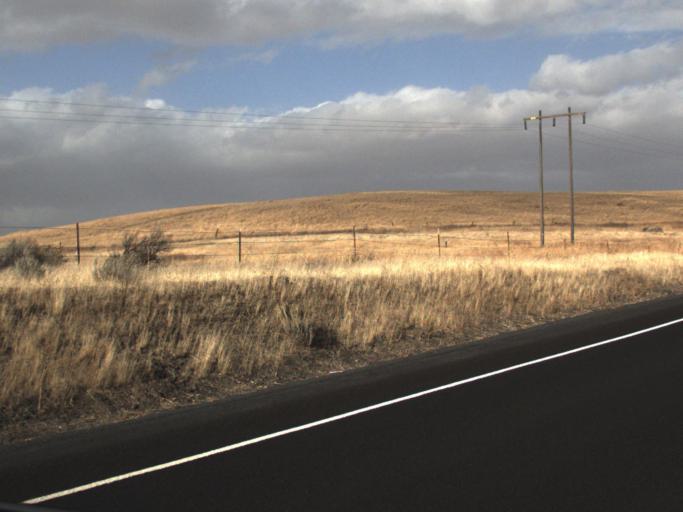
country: US
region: Washington
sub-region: Lincoln County
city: Davenport
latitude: 47.5286
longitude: -118.2036
